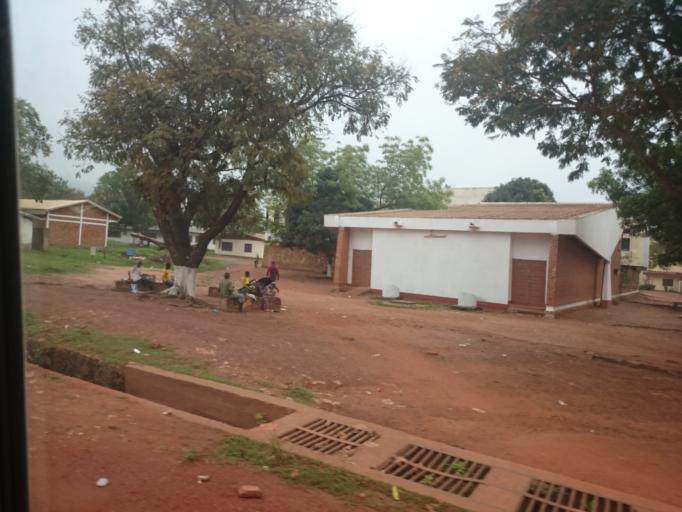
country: CF
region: Bangui
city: Bangui
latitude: 4.3791
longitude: 18.5612
